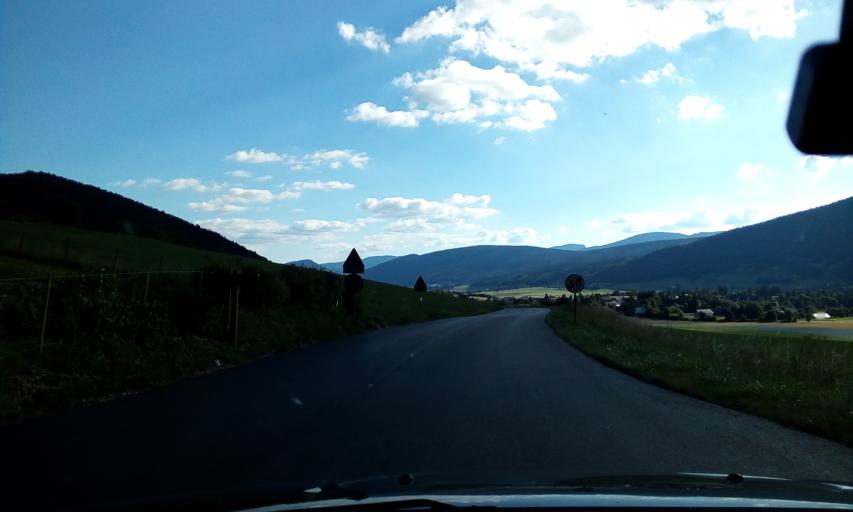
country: FR
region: Rhone-Alpes
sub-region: Departement de l'Isere
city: Lans-en-Vercors
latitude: 45.1330
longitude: 5.6032
